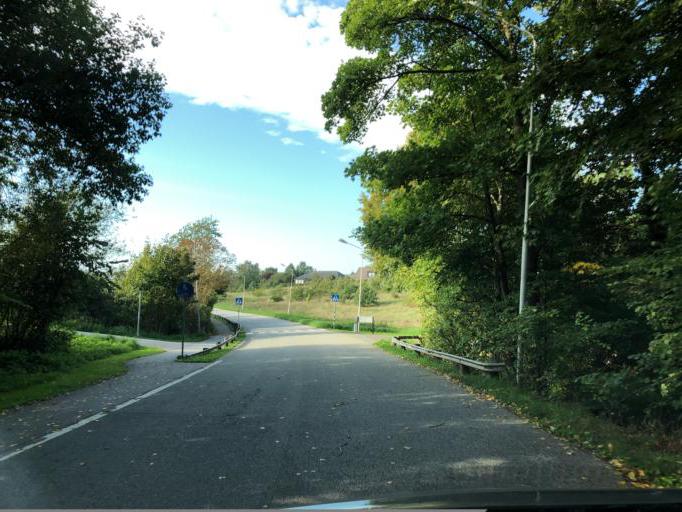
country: SE
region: Skane
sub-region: Kavlinge Kommun
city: Kaevlinge
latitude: 55.7756
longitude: 13.1101
